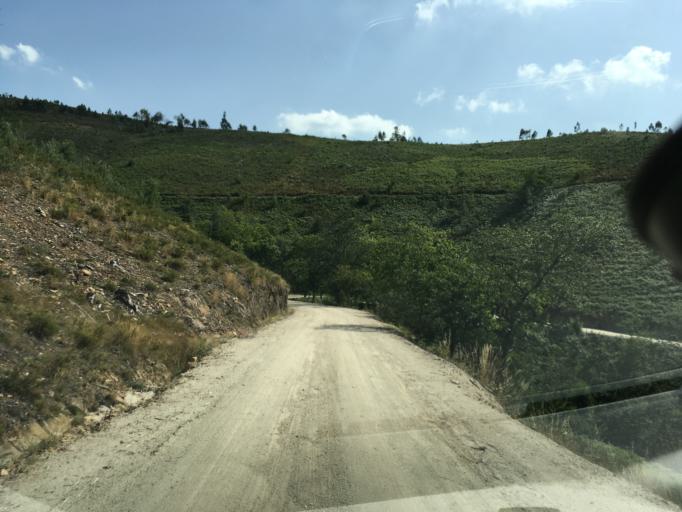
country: PT
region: Braga
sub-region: Celorico de Basto
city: Celorico de Basto
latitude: 41.2982
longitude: -7.9847
